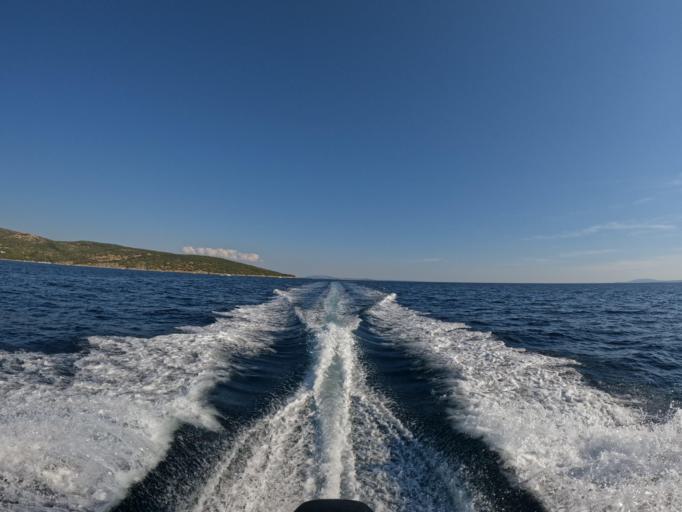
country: HR
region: Primorsko-Goranska
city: Punat
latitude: 44.9921
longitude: 14.6049
